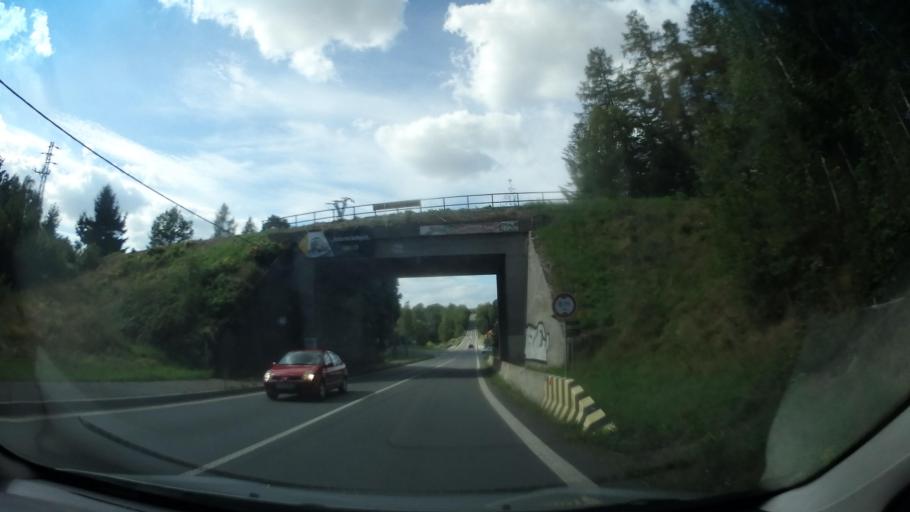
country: CZ
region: Vysocina
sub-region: Okres Zd'ar nad Sazavou
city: Nove Veseli
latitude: 49.5597
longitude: 15.8641
